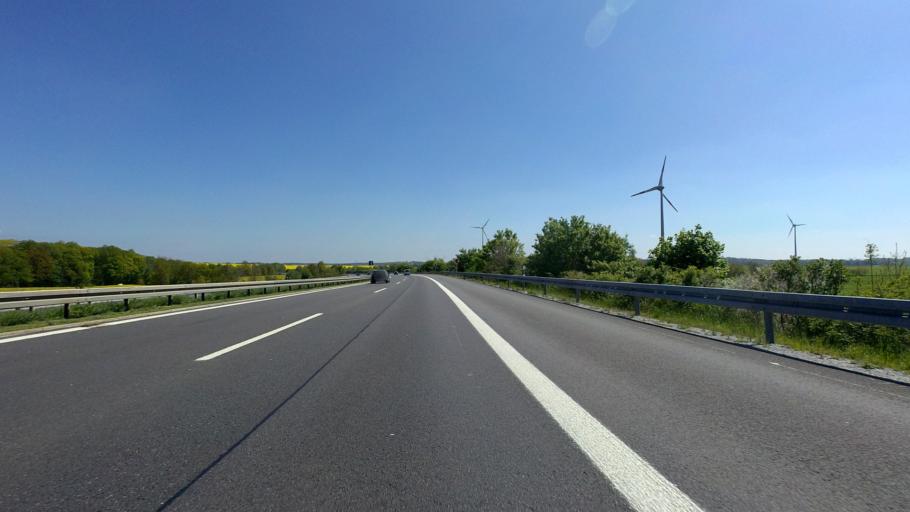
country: DE
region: Saxony
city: Wachau
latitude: 51.1637
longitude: 13.9238
